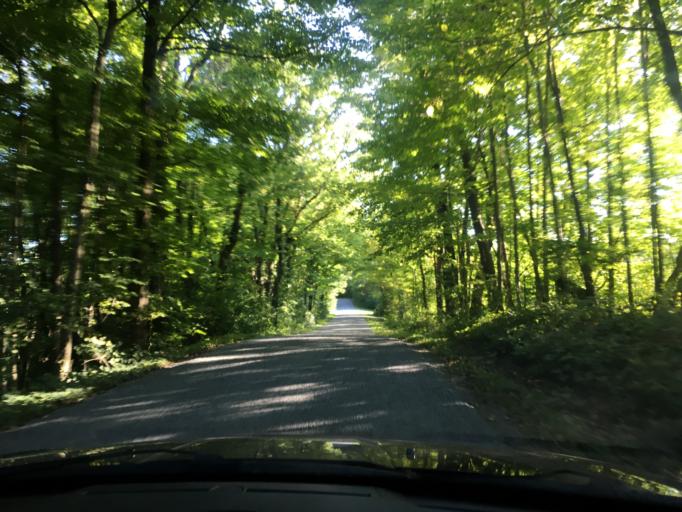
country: US
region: Ohio
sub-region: Logan County
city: West Liberty
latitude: 40.2588
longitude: -83.6622
